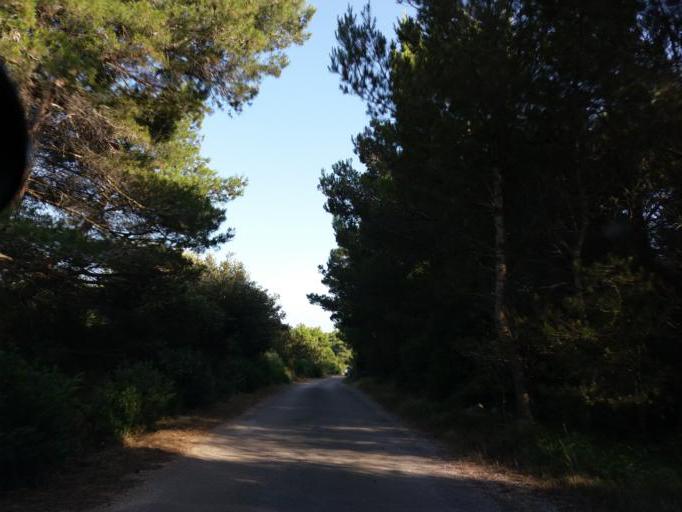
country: HR
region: Zadarska
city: Ugljan
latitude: 44.1380
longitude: 14.8526
